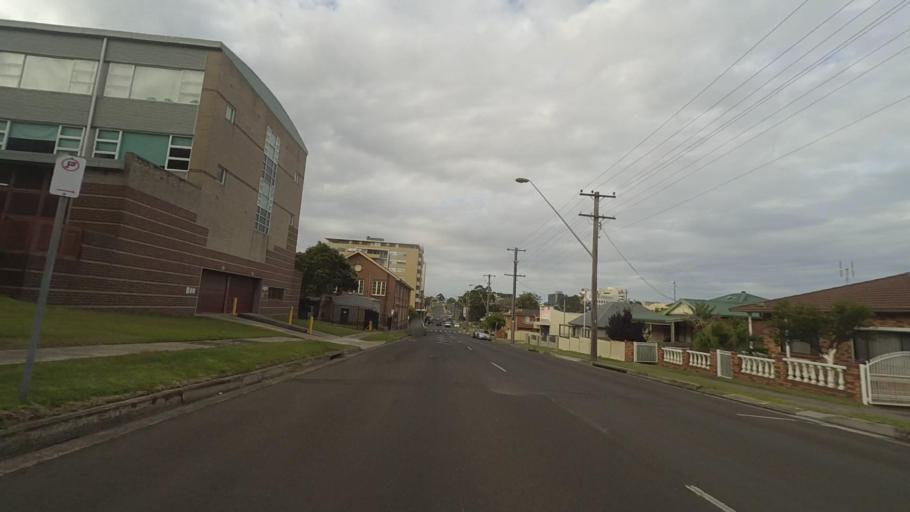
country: AU
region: New South Wales
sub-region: Wollongong
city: Wollongong
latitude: -34.4297
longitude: 150.8865
